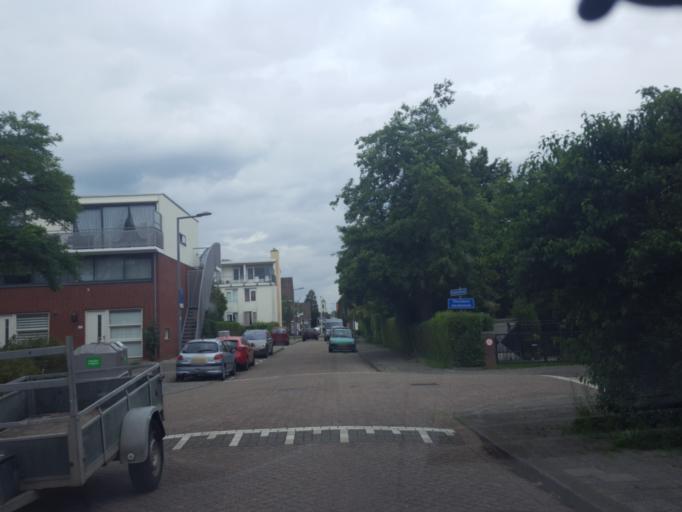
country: NL
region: South Holland
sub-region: Gemeente Schiedam
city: Schiedam
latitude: 51.9372
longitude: 4.4256
